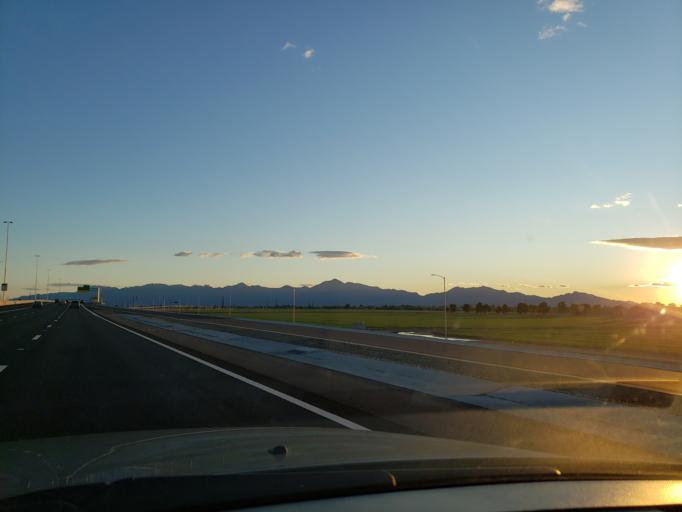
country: US
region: Arizona
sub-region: Maricopa County
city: Laveen
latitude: 33.4339
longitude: -112.1874
